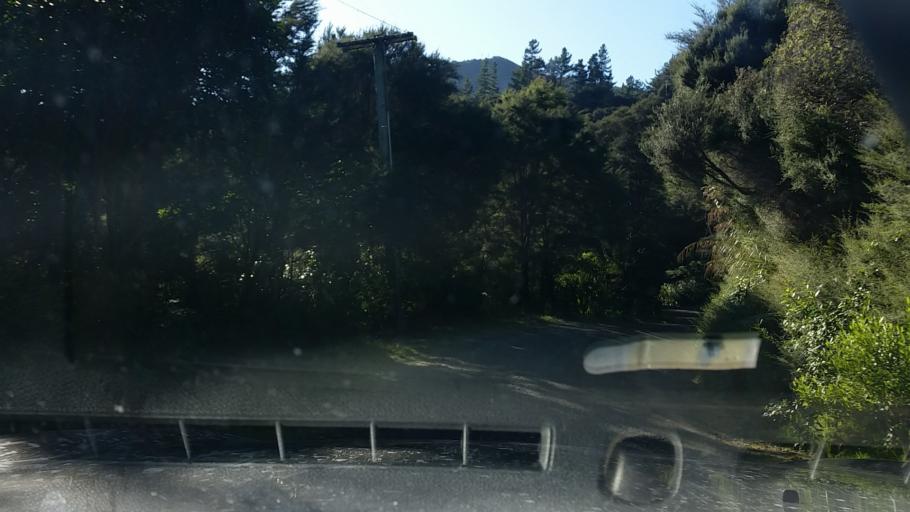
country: NZ
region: Marlborough
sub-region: Marlborough District
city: Picton
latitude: -41.1794
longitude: 173.9730
